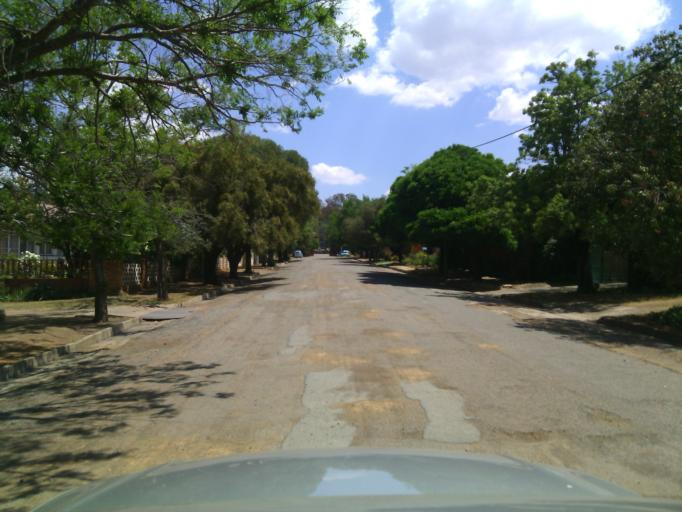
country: ZA
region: Orange Free State
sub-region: Xhariep District Municipality
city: Dewetsdorp
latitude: -29.5834
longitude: 26.6620
